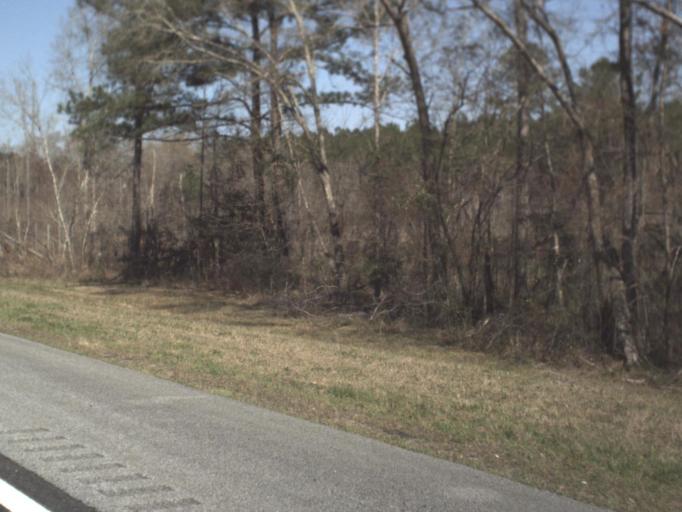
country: US
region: Florida
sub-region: Jackson County
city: Sneads
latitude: 30.6392
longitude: -84.9575
